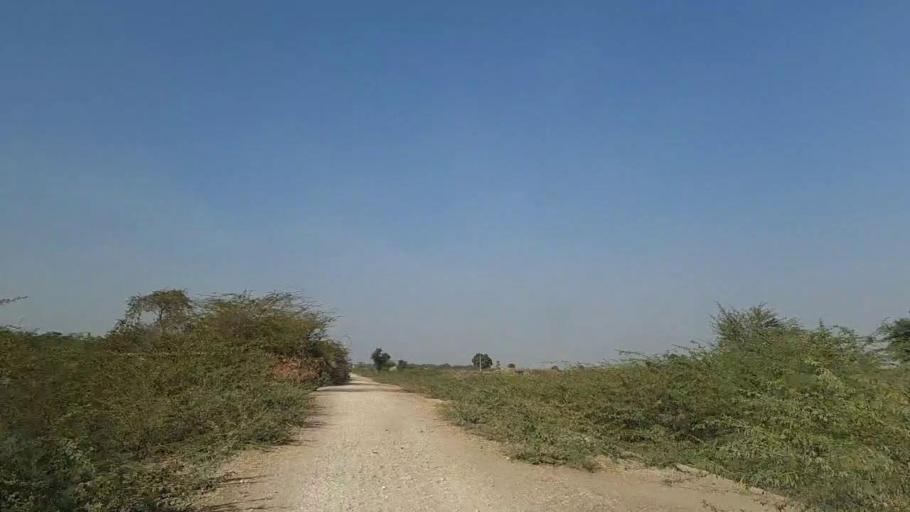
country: PK
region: Sindh
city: Naukot
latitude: 24.9453
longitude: 69.4839
